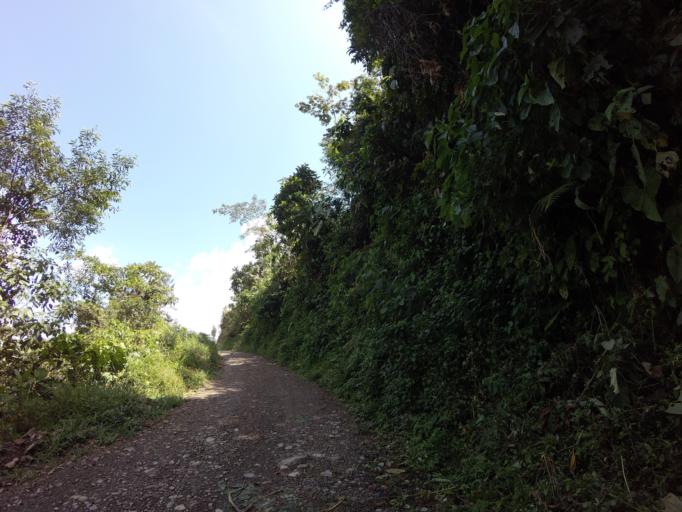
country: CO
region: Caldas
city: Pensilvania
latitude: 5.4885
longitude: -75.1853
